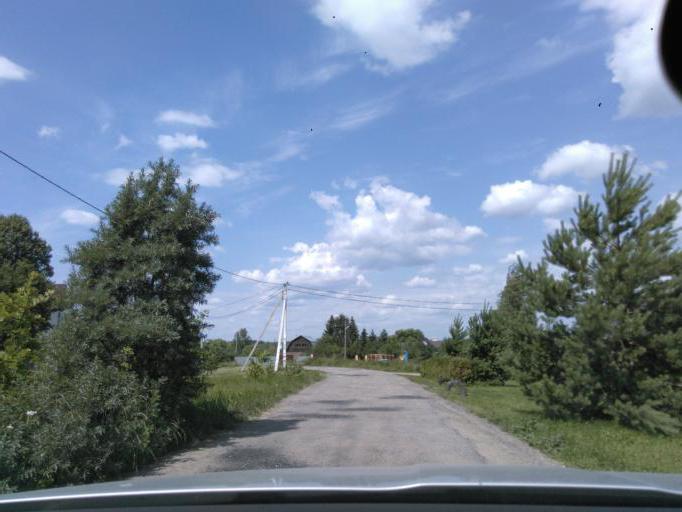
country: RU
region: Moskovskaya
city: Solnechnogorsk
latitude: 56.1315
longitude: 36.9630
